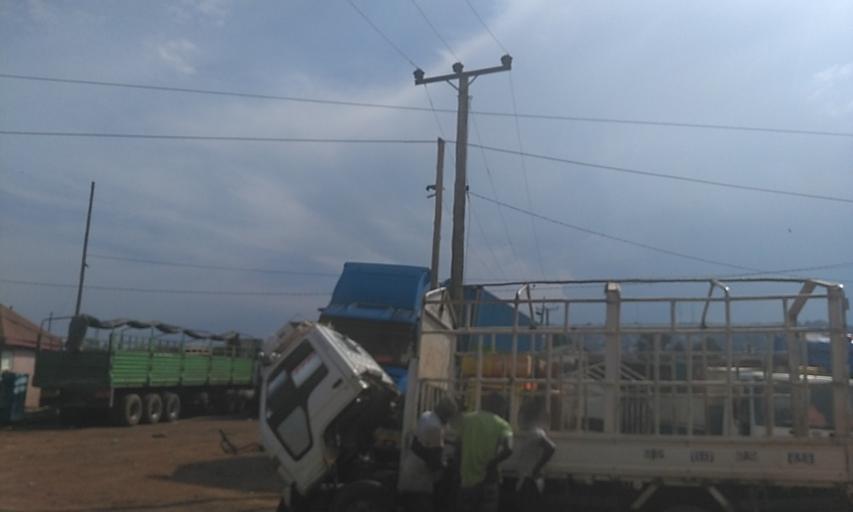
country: UG
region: Central Region
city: Kampala Central Division
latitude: 0.2969
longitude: 32.5413
